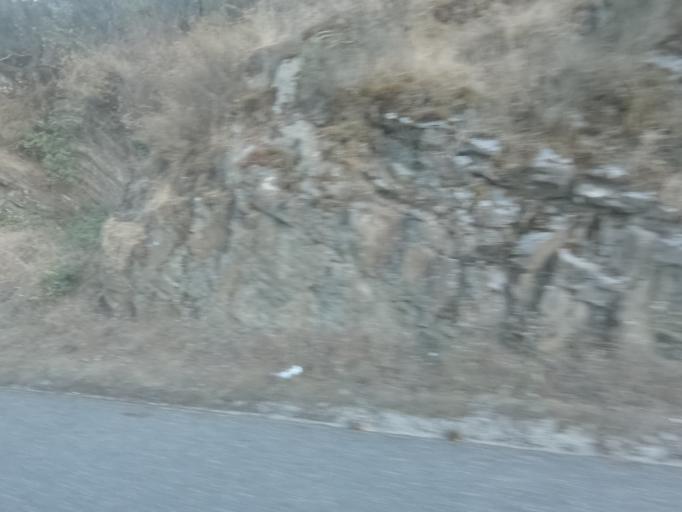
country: PT
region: Vila Real
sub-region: Peso da Regua
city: Peso da Regua
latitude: 41.1440
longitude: -7.7365
